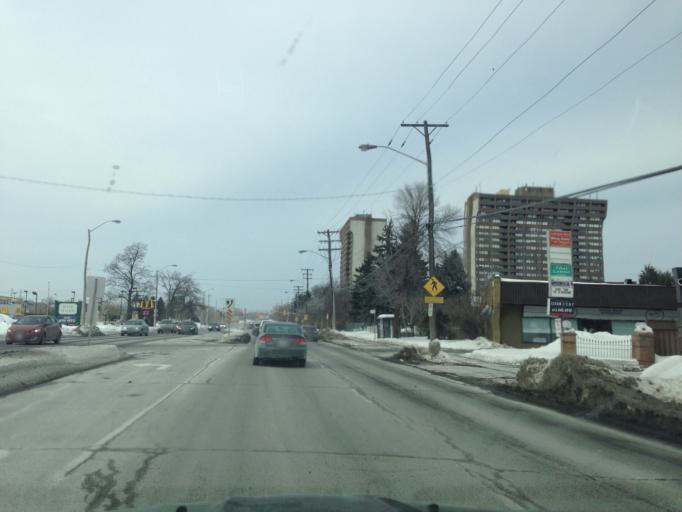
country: CA
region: Ontario
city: Ottawa
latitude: 45.3543
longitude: -75.6490
